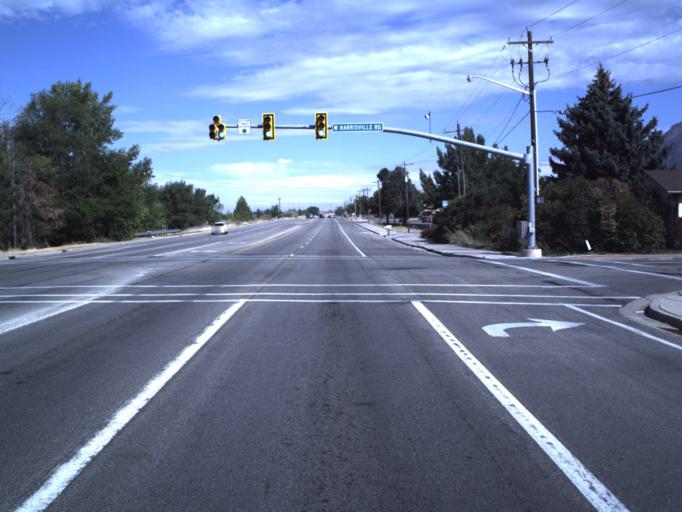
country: US
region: Utah
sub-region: Weber County
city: Harrisville
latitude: 41.2812
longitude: -111.9855
